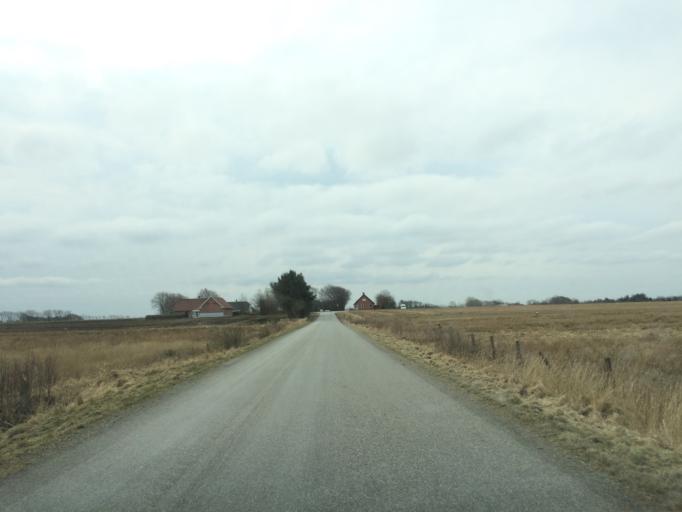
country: DK
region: South Denmark
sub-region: Varde Kommune
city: Oksbol
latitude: 55.7932
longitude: 8.3590
